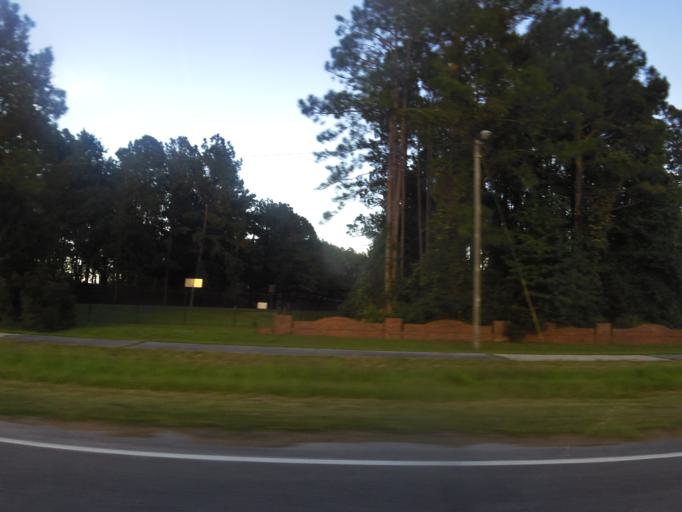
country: US
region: Georgia
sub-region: Camden County
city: Kings Bay Base
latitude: 30.7831
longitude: -81.5765
